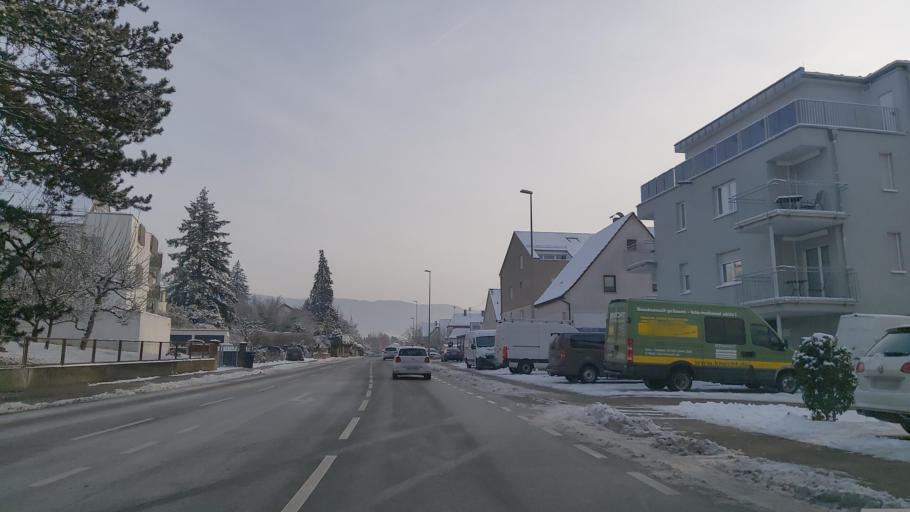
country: DE
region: Baden-Wuerttemberg
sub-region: Tuebingen Region
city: Metzingen
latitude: 48.5465
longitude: 9.2879
